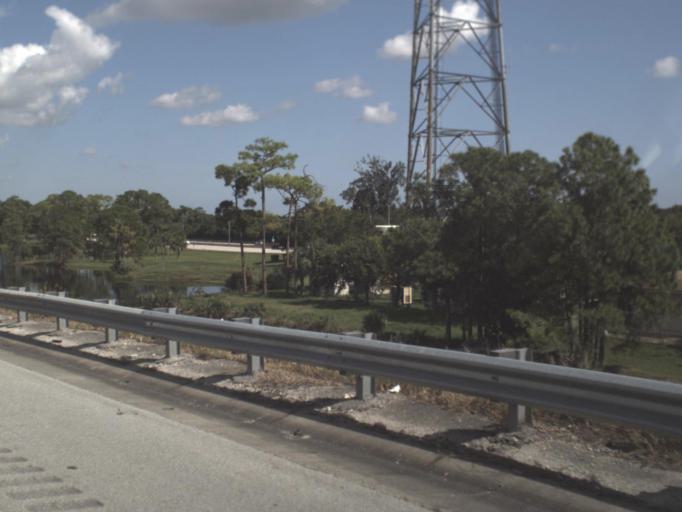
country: US
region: Florida
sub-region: Palm Beach County
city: Boca Del Mar
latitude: 26.3693
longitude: -80.1707
